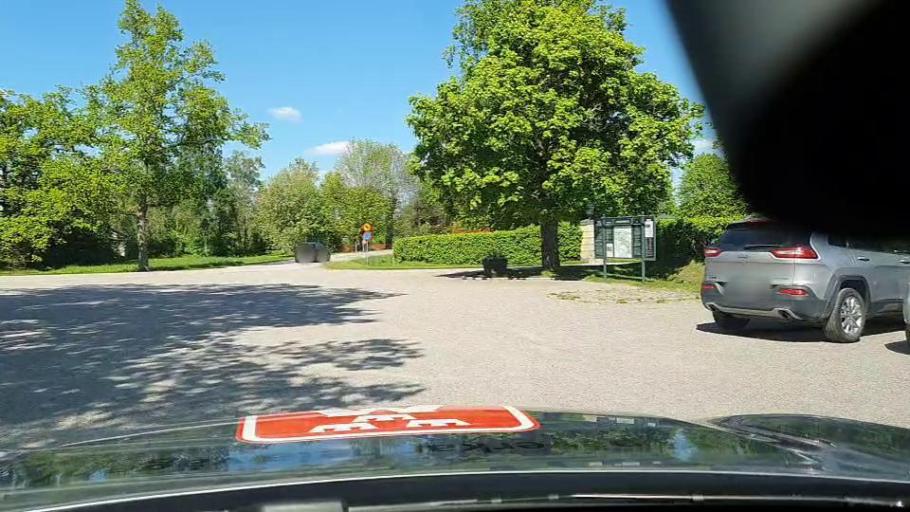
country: SE
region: Vaestmanland
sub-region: Hallstahammars Kommun
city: Kolback
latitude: 59.5246
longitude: 16.2650
